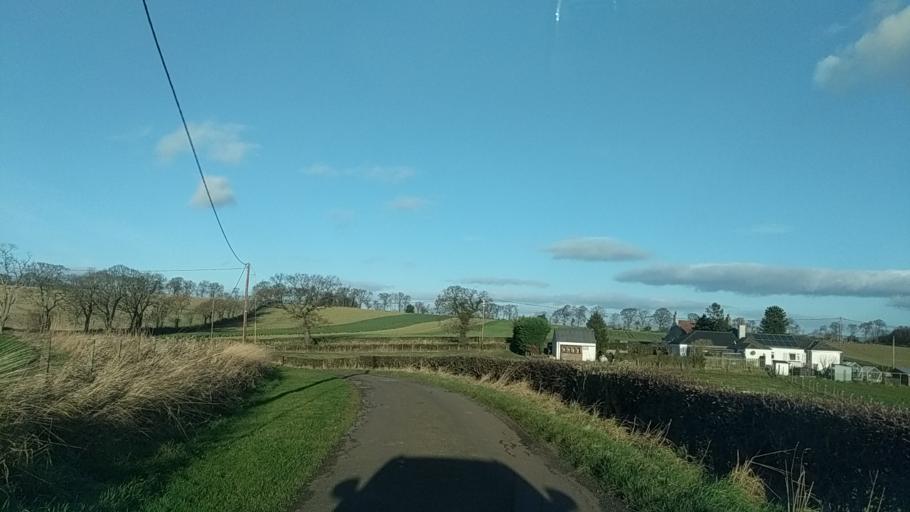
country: GB
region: Scotland
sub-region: West Lothian
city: Linlithgow
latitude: 55.9966
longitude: -3.5445
